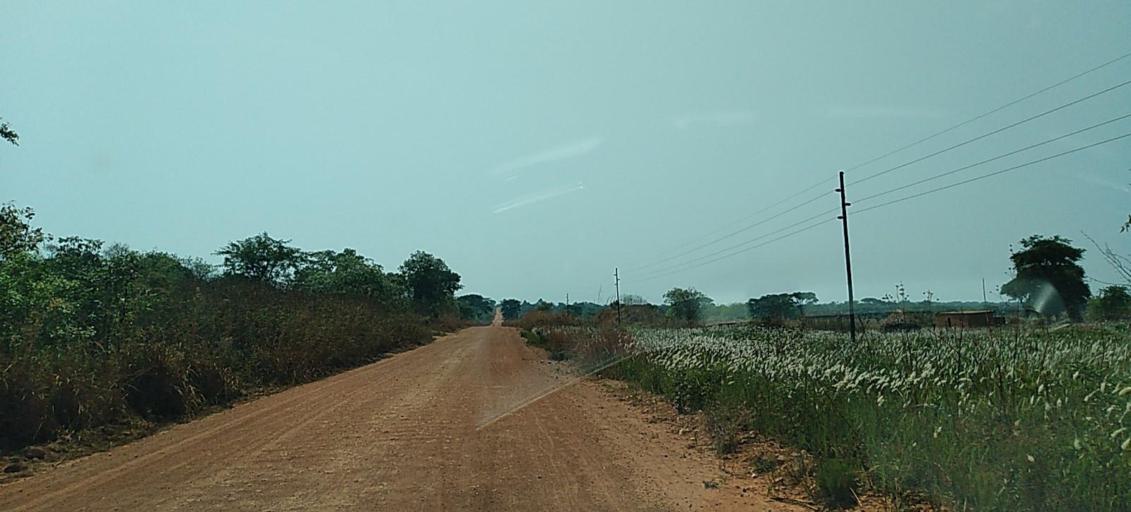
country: ZM
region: North-Western
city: Kansanshi
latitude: -12.0049
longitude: 26.5643
